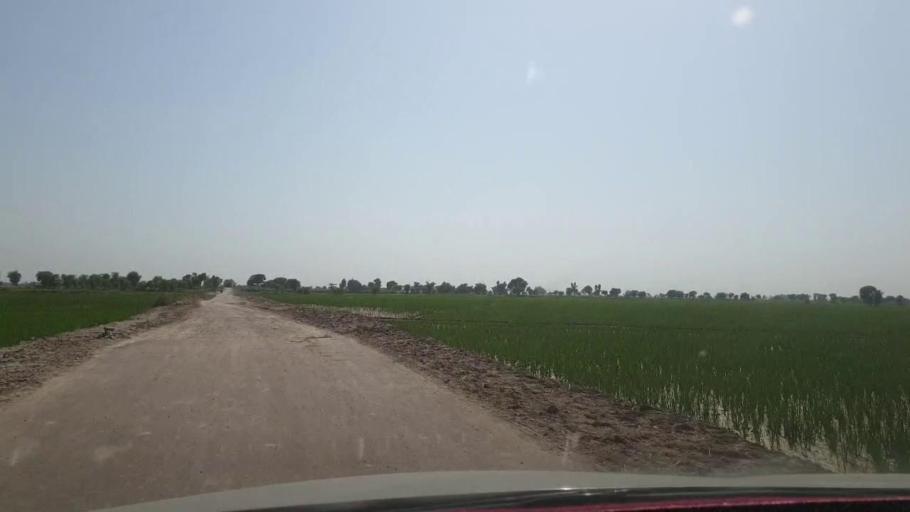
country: PK
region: Sindh
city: Nasirabad
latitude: 27.3563
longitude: 67.8458
